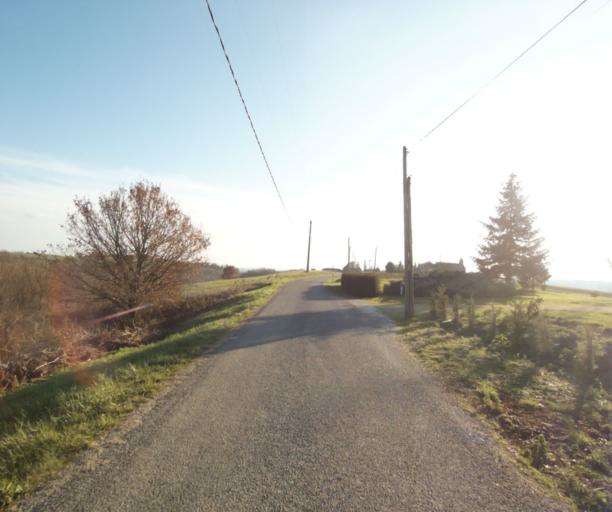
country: FR
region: Midi-Pyrenees
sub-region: Departement du Tarn-et-Garonne
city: Moissac
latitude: 44.1400
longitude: 1.1117
